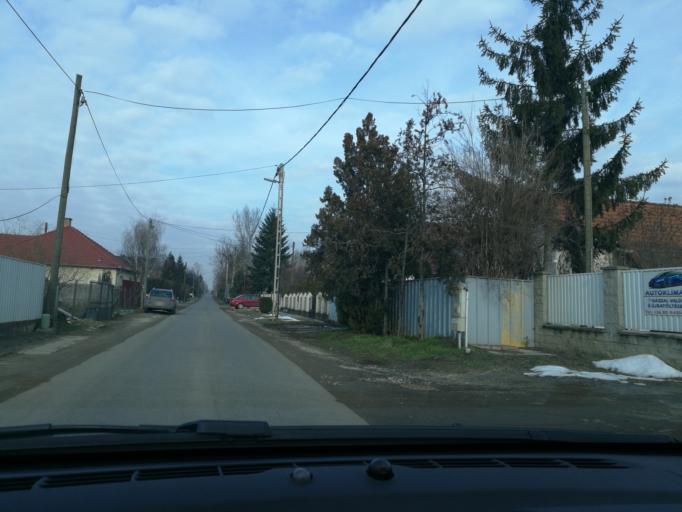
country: HU
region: Szabolcs-Szatmar-Bereg
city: Nyiregyhaza
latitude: 47.9346
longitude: 21.7371
